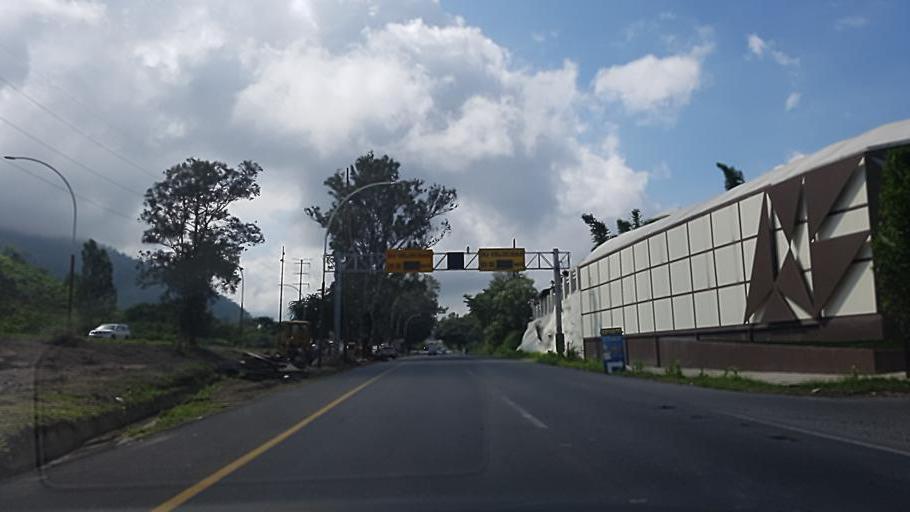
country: MX
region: Nayarit
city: Tepic
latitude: 21.4948
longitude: -104.9064
